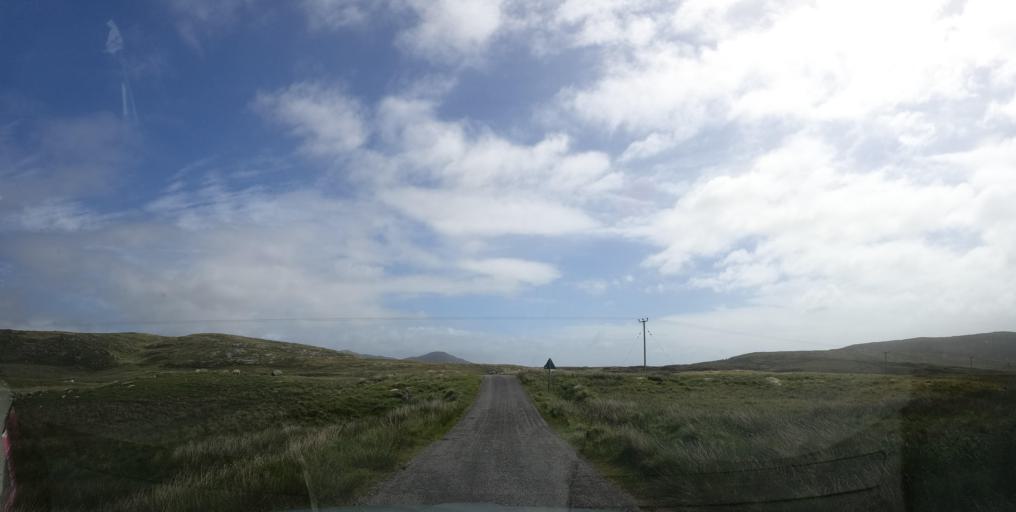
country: GB
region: Scotland
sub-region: Eilean Siar
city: Isle of South Uist
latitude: 57.1379
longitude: -7.3653
